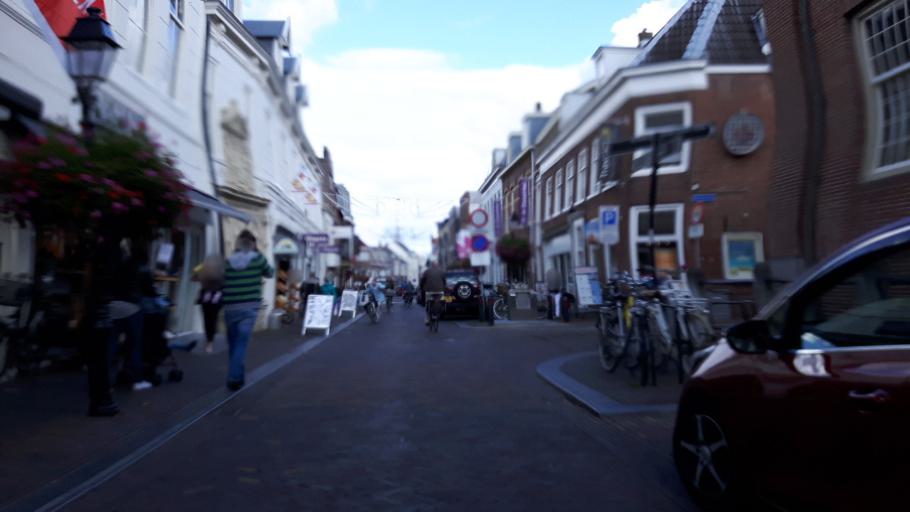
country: NL
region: South Holland
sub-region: Gemeente Leerdam
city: Leerdam
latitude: 51.8904
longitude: 5.0919
